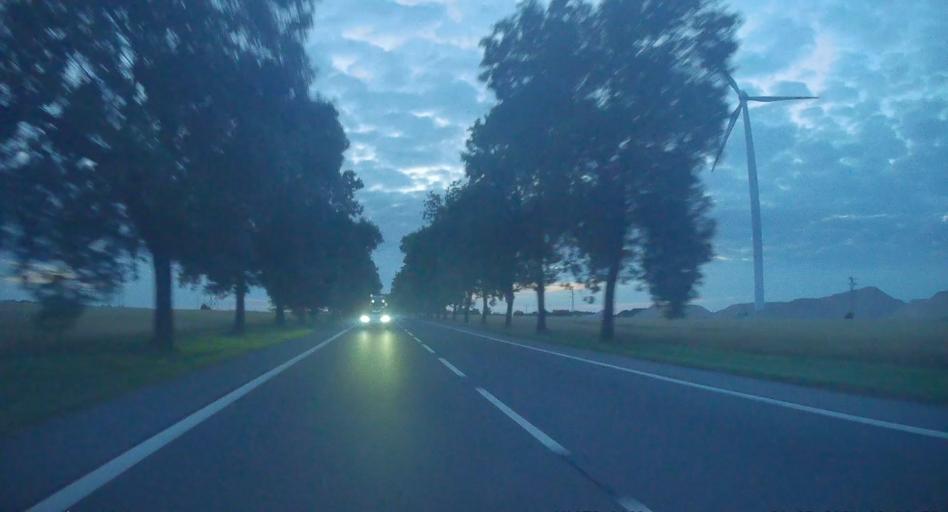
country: PL
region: Silesian Voivodeship
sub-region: Powiat klobucki
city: Klobuck
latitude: 50.9144
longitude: 18.8961
